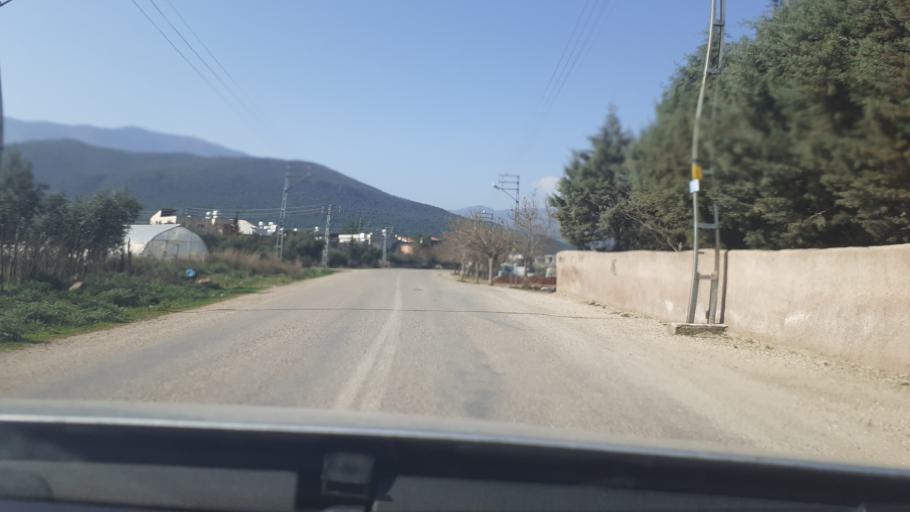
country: TR
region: Hatay
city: Aktepe
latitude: 36.7086
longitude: 36.4873
